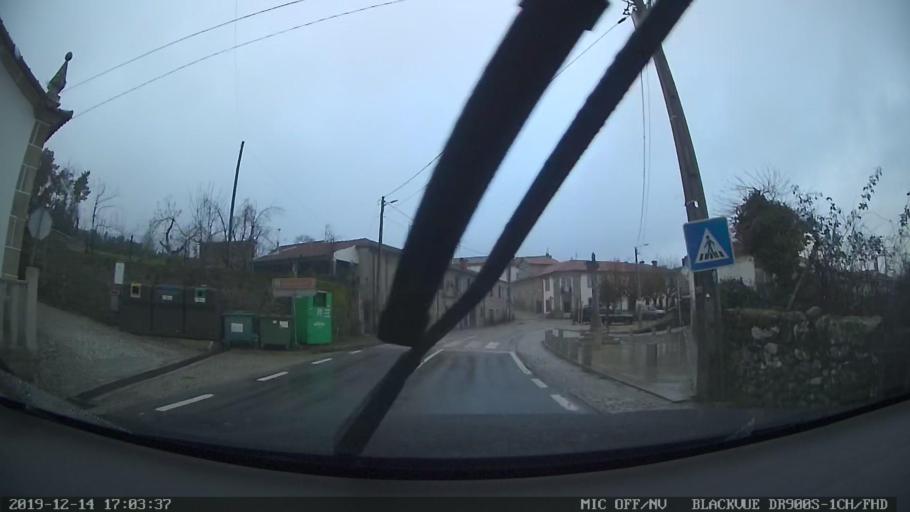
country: PT
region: Vila Real
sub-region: Vila Pouca de Aguiar
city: Vila Pouca de Aguiar
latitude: 41.4438
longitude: -7.5714
